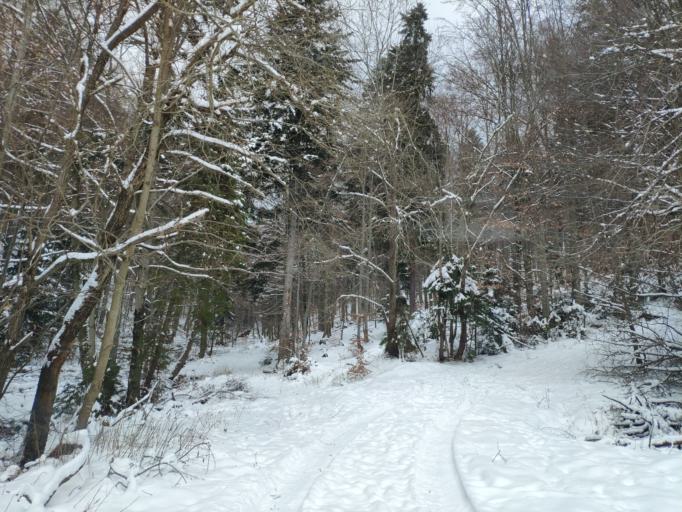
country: SK
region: Kosicky
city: Gelnica
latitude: 48.7664
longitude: 20.9603
